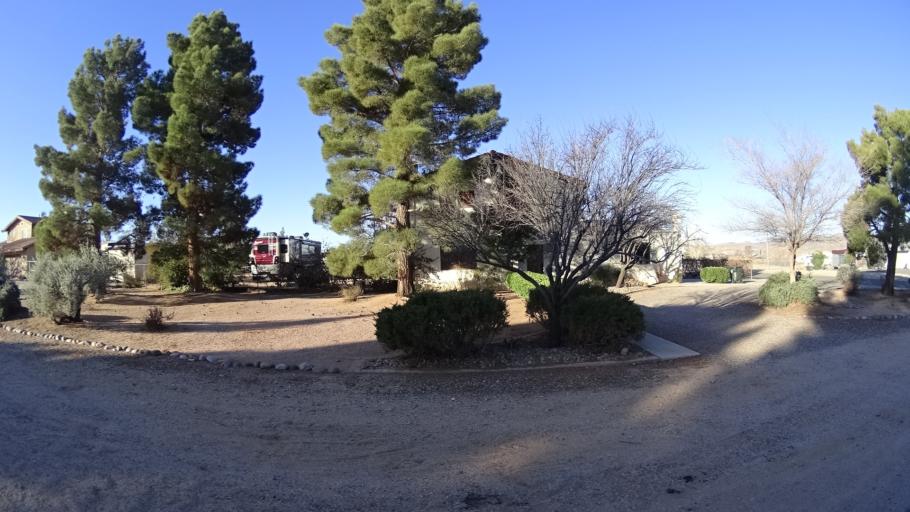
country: US
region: Arizona
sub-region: Mohave County
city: Kingman
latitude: 35.2060
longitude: -114.0092
